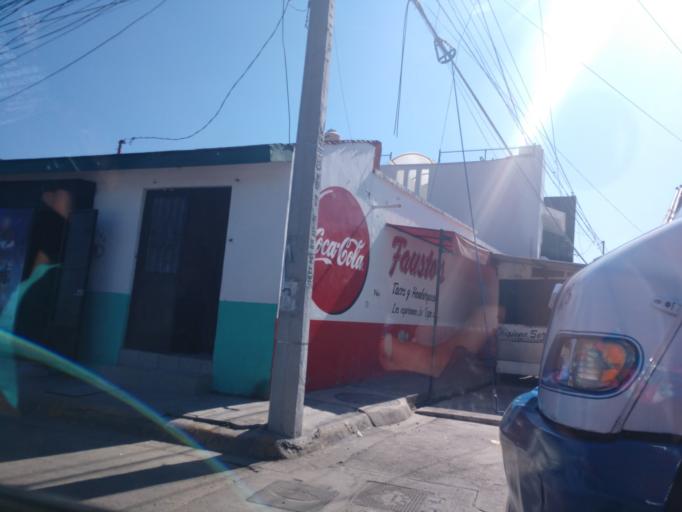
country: MX
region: Nayarit
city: Xalisco
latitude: 21.4689
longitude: -104.8746
